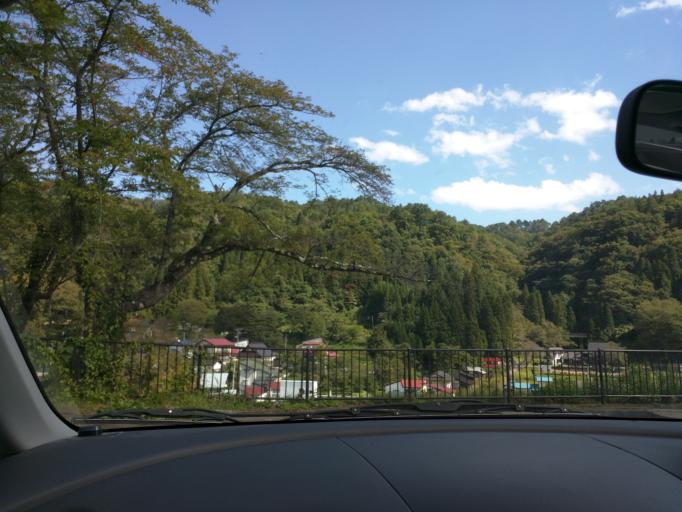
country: JP
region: Fukushima
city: Kitakata
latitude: 37.5306
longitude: 139.7247
